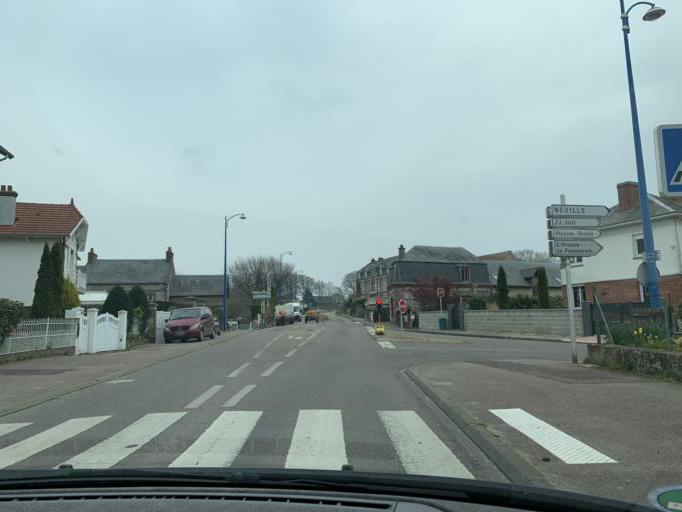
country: FR
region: Haute-Normandie
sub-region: Departement de la Seine-Maritime
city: Saint-Valery-en-Caux
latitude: 49.8606
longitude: 0.7173
